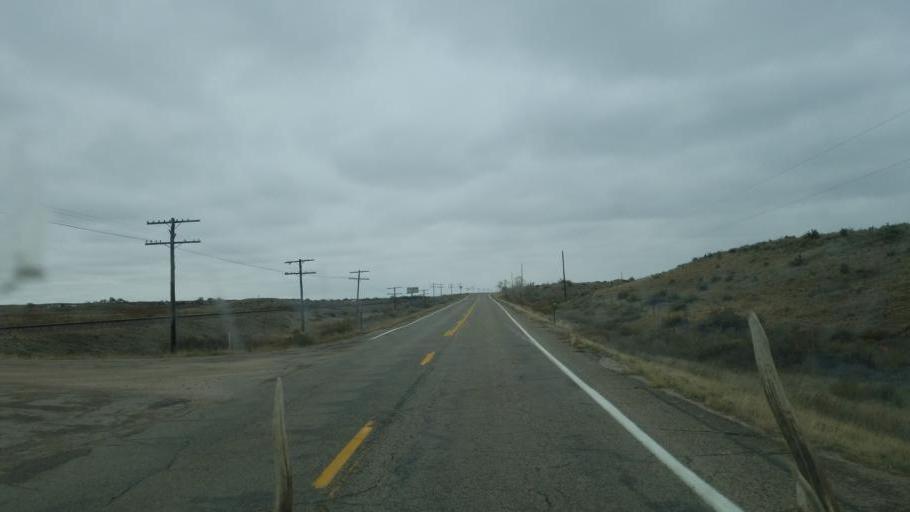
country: US
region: Colorado
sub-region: Otero County
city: Fowler
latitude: 38.2509
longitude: -104.2748
